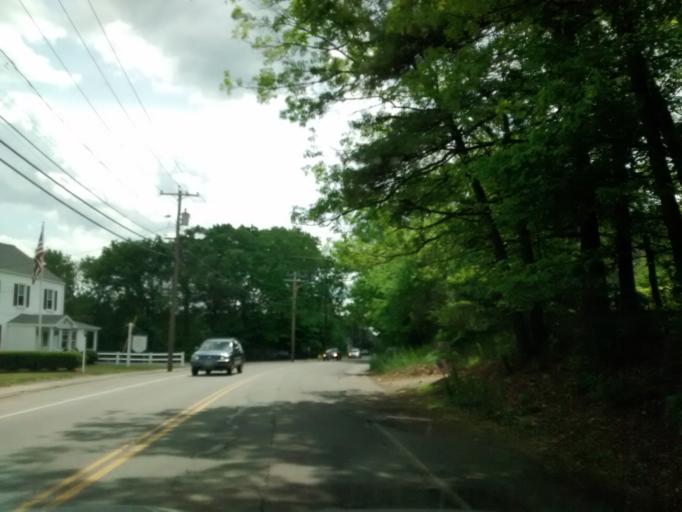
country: US
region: Massachusetts
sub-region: Worcester County
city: Whitinsville
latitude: 42.1191
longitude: -71.6505
